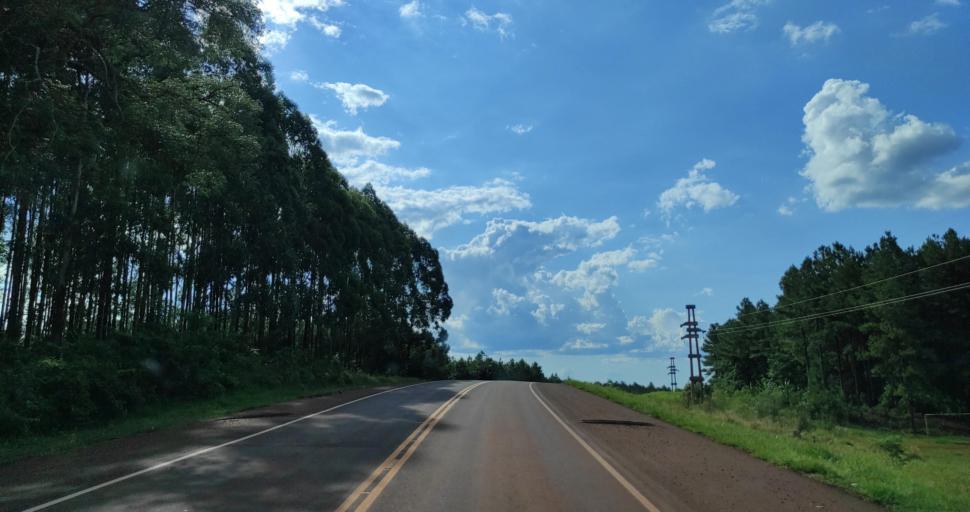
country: AR
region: Misiones
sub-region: Departamento de San Pedro
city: San Pedro
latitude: -26.3689
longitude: -53.9434
